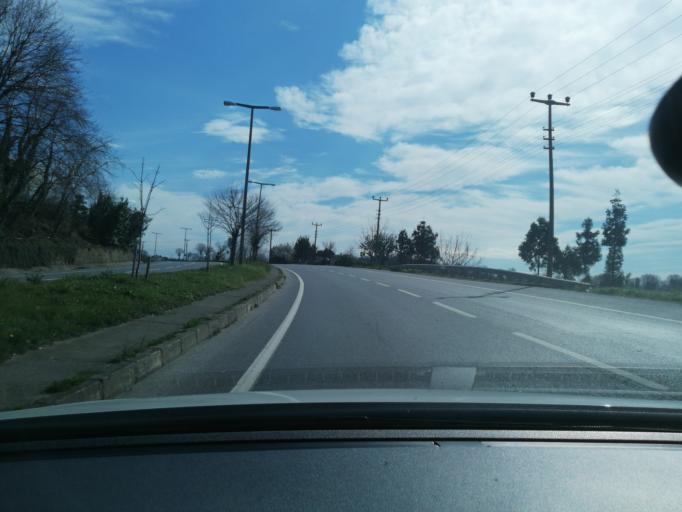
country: TR
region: Duzce
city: Akcakoca
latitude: 41.0834
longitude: 31.1568
